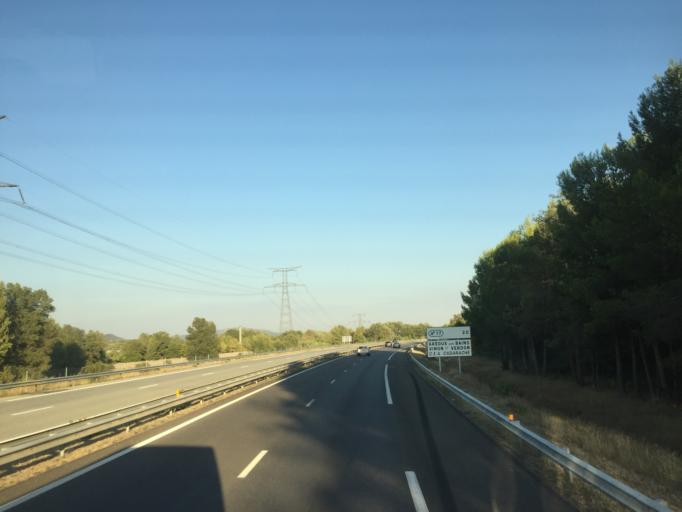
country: FR
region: Provence-Alpes-Cote d'Azur
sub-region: Departement des Bouches-du-Rhone
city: Meyrargues
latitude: 43.6613
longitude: 5.5127
